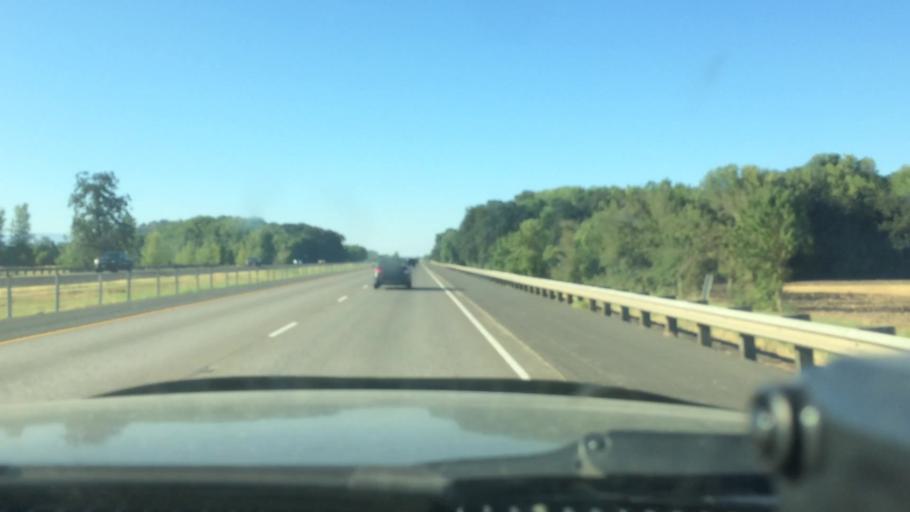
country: US
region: Oregon
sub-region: Linn County
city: Tangent
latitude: 44.4793
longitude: -123.0628
